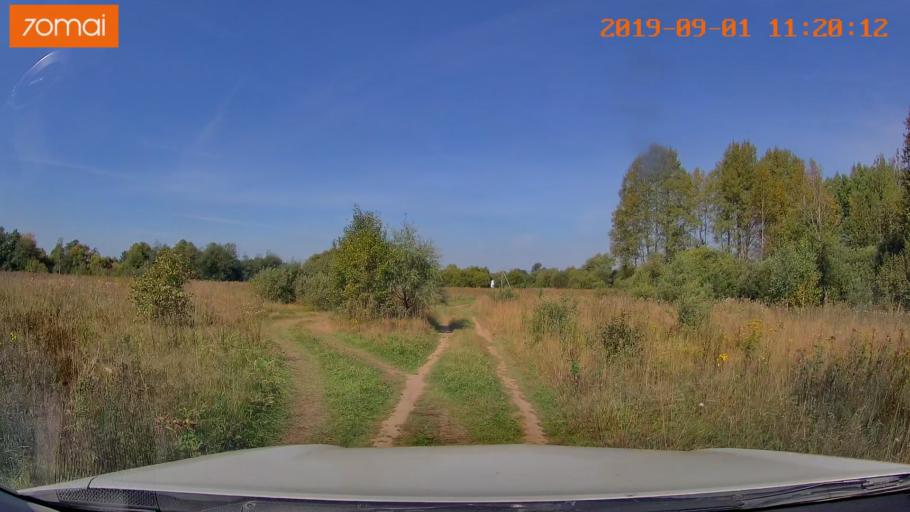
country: RU
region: Kaluga
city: Detchino
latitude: 54.8290
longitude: 36.3614
